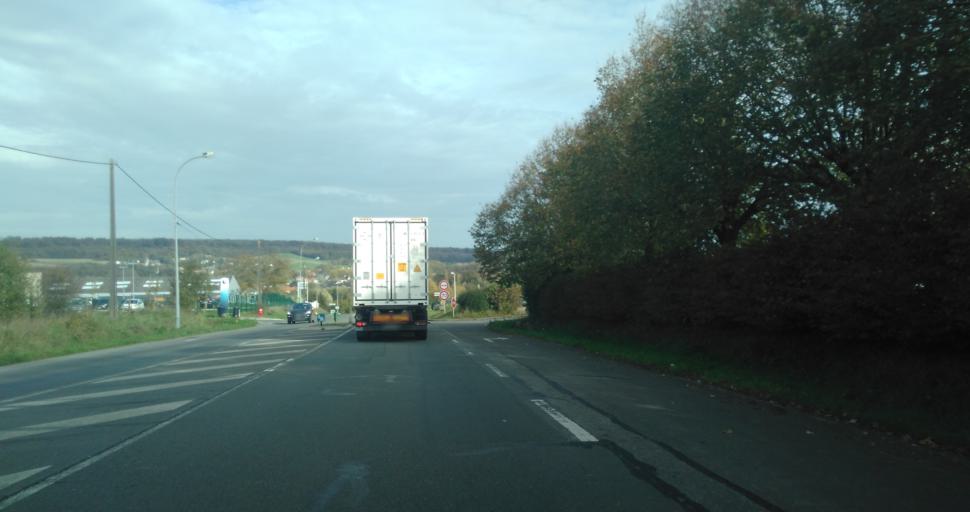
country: FR
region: Nord-Pas-de-Calais
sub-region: Departement du Pas-de-Calais
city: Hesdin
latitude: 50.3667
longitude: 2.0263
